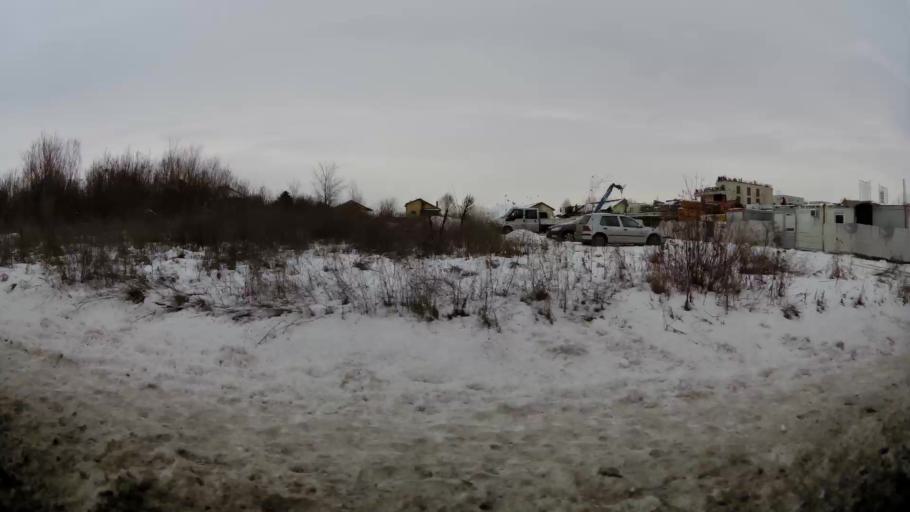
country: RO
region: Ilfov
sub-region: Comuna Tunari
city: Tunari
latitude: 44.5248
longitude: 26.1433
